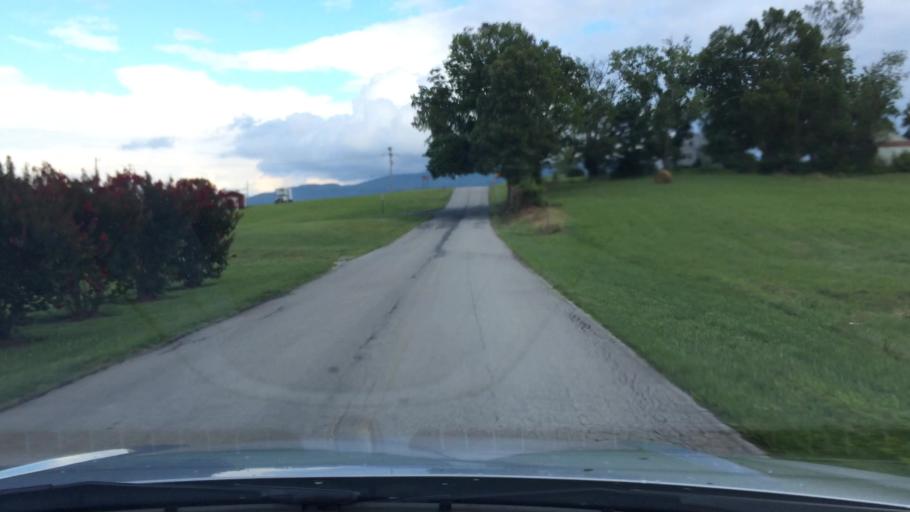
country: US
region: Tennessee
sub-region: Blount County
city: Wildwood
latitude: 35.7563
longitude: -83.8879
